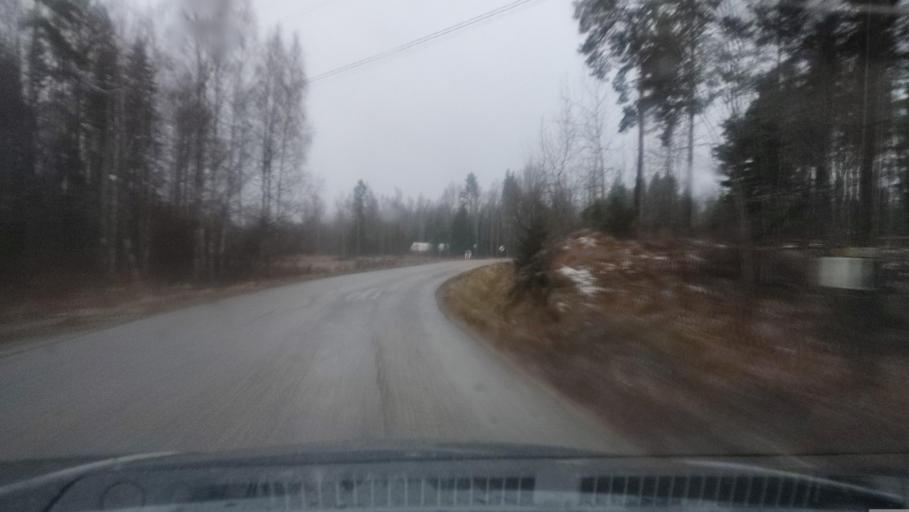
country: FI
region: Southern Ostrobothnia
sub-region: Suupohja
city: Karijoki
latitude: 62.1407
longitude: 21.5726
